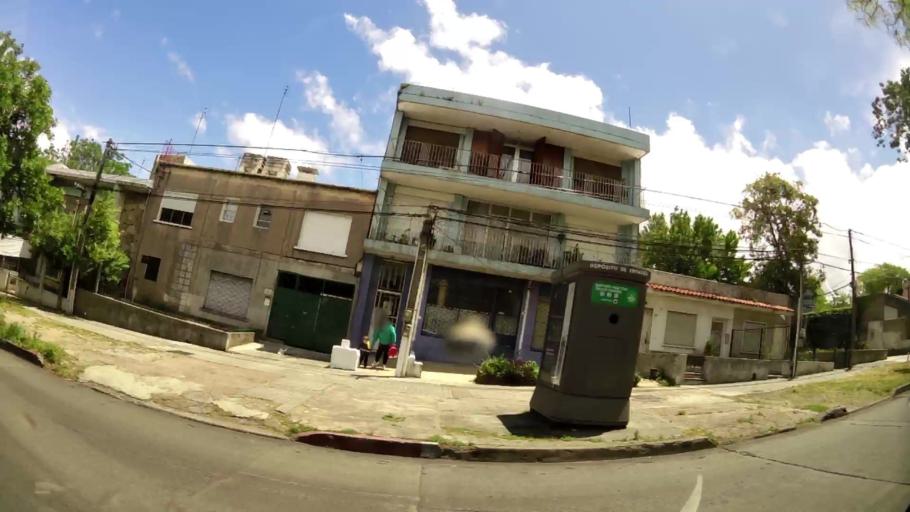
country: UY
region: Montevideo
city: Montevideo
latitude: -34.8573
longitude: -56.1844
